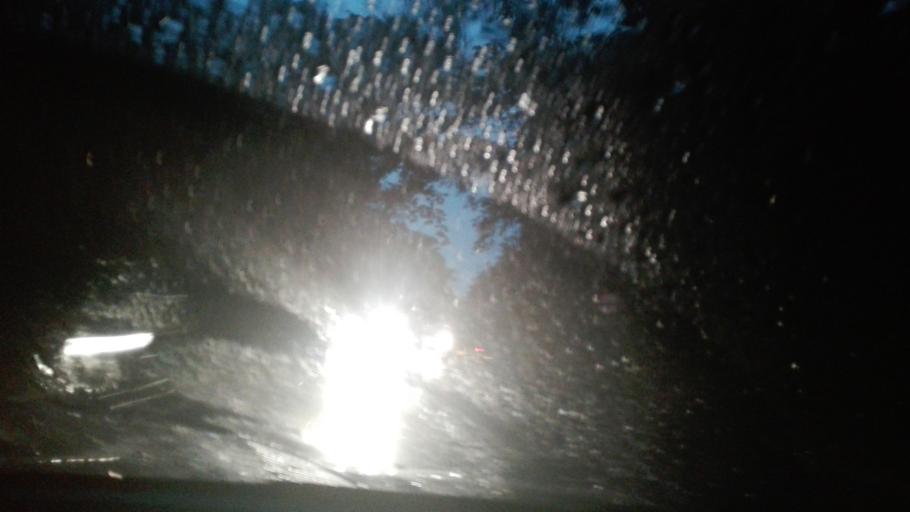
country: CO
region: Quindio
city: Montenegro
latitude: 4.5476
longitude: -75.7426
